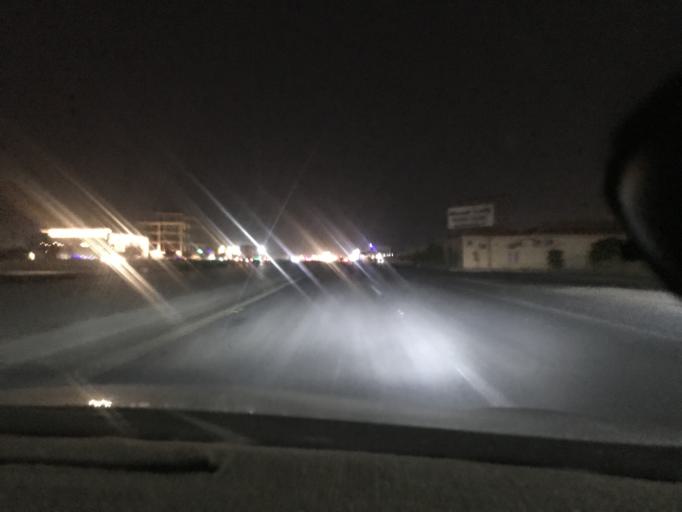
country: SA
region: Ar Riyad
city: Riyadh
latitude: 24.8415
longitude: 46.6069
